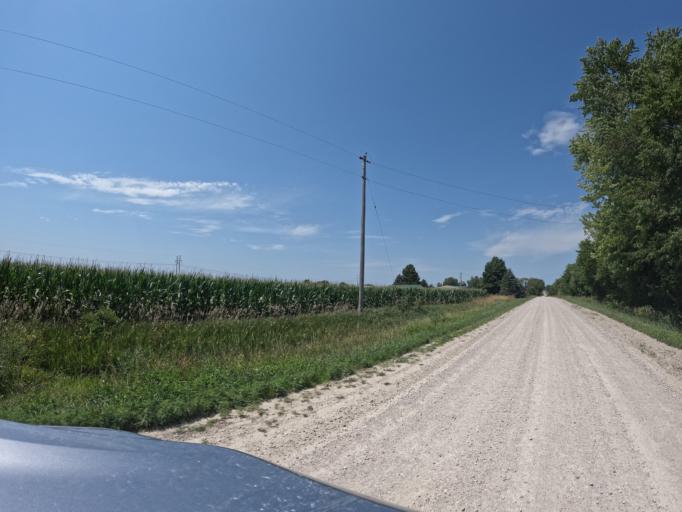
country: US
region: Iowa
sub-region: Henry County
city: Mount Pleasant
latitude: 40.9100
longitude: -91.6364
